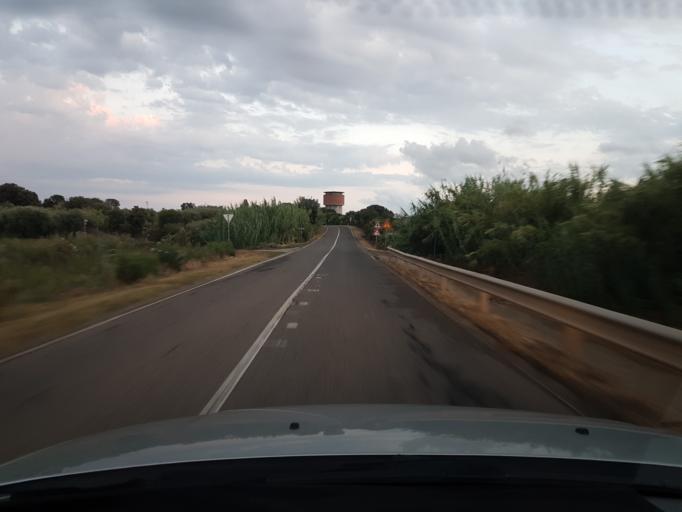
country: IT
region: Sardinia
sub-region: Provincia di Oristano
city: Tramatza
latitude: 40.0093
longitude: 8.6463
